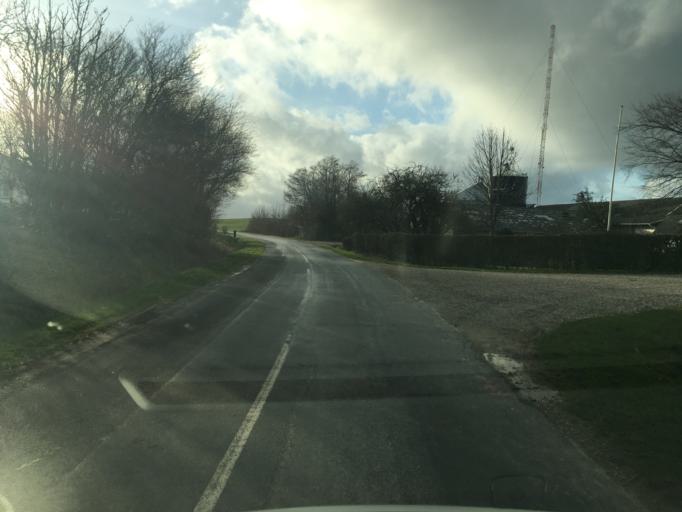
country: DK
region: South Denmark
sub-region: Sonderborg Kommune
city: Grasten
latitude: 54.9642
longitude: 9.5597
